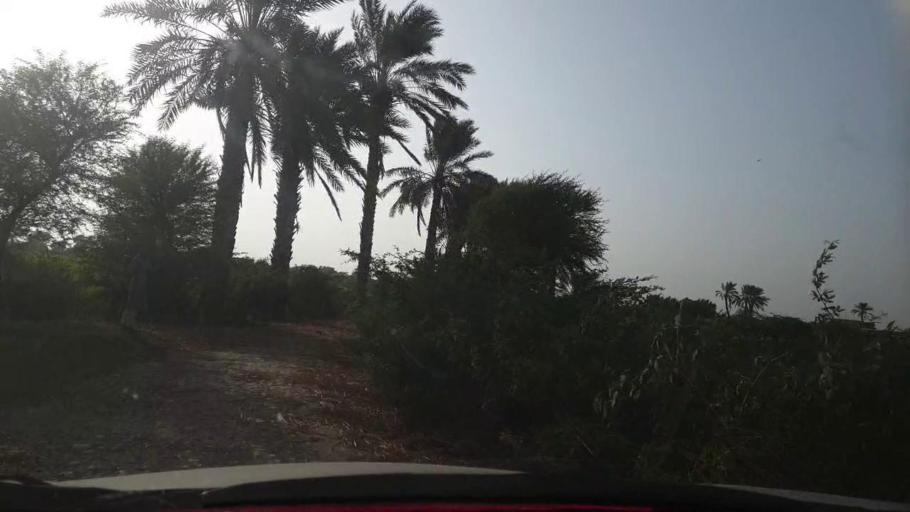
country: PK
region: Sindh
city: Talhar
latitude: 24.9036
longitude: 68.8217
